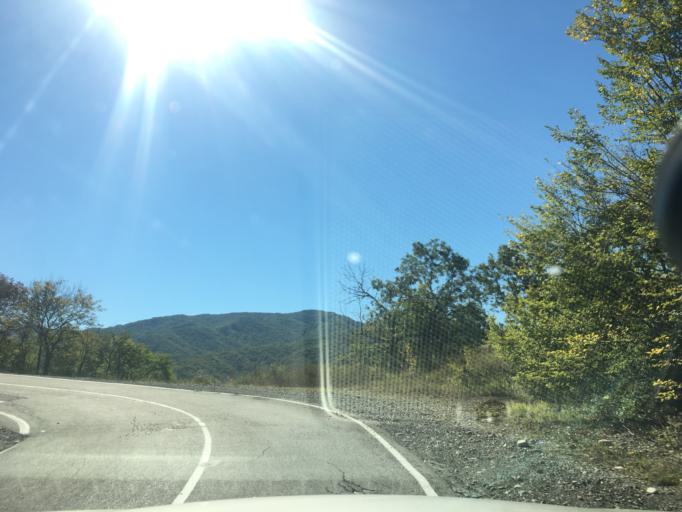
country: GE
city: Didi Lilo
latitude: 41.8663
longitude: 44.9169
